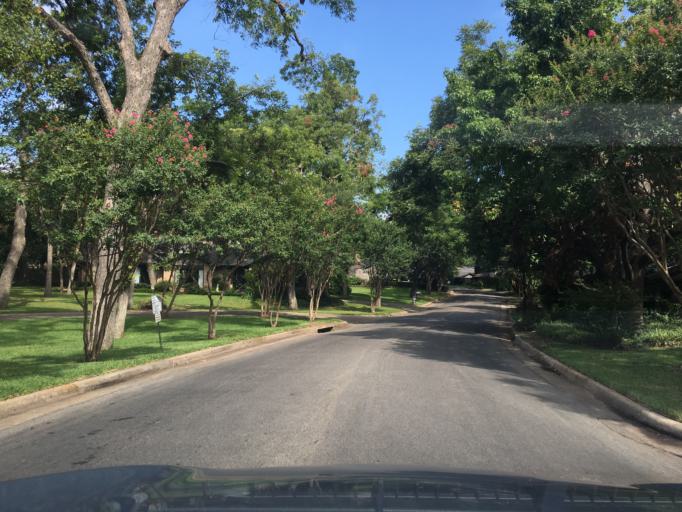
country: US
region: Texas
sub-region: Dallas County
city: Richardson
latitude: 32.9191
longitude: -96.7830
